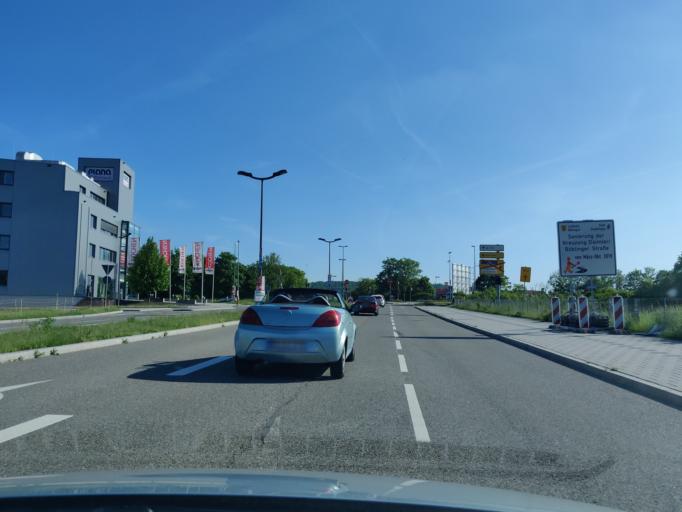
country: DE
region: Baden-Wuerttemberg
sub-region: Regierungsbezirk Stuttgart
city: Boeblingen
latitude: 48.6879
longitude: 8.9873
